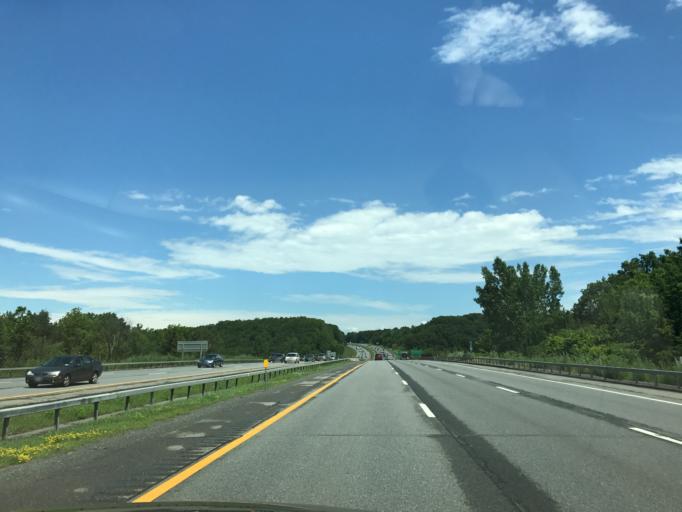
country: US
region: New York
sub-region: Saratoga County
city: Country Knolls
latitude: 42.9495
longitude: -73.8045
